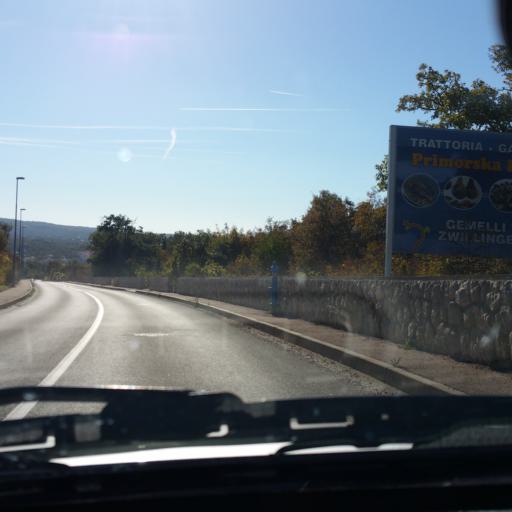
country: HR
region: Primorsko-Goranska
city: Njivice
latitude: 45.1308
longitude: 14.5405
